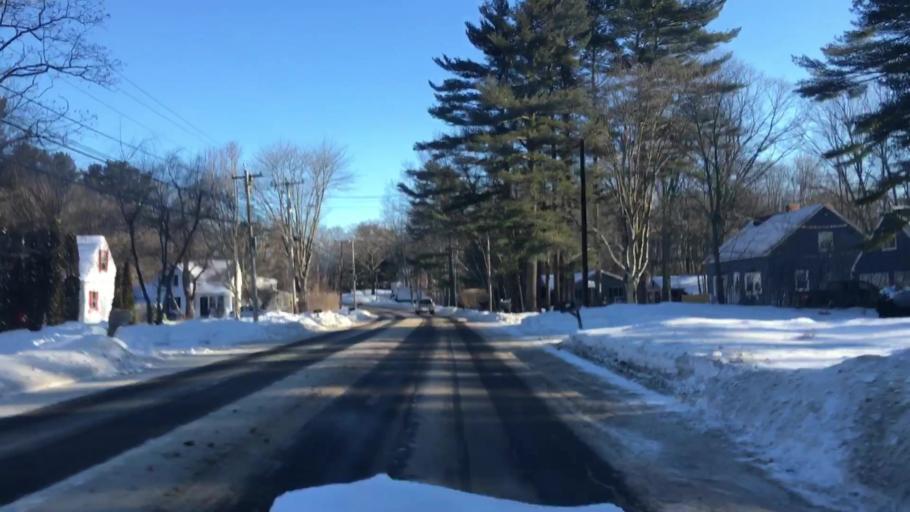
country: US
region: Maine
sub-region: Cumberland County
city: Brunswick
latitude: 43.9290
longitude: -69.9441
